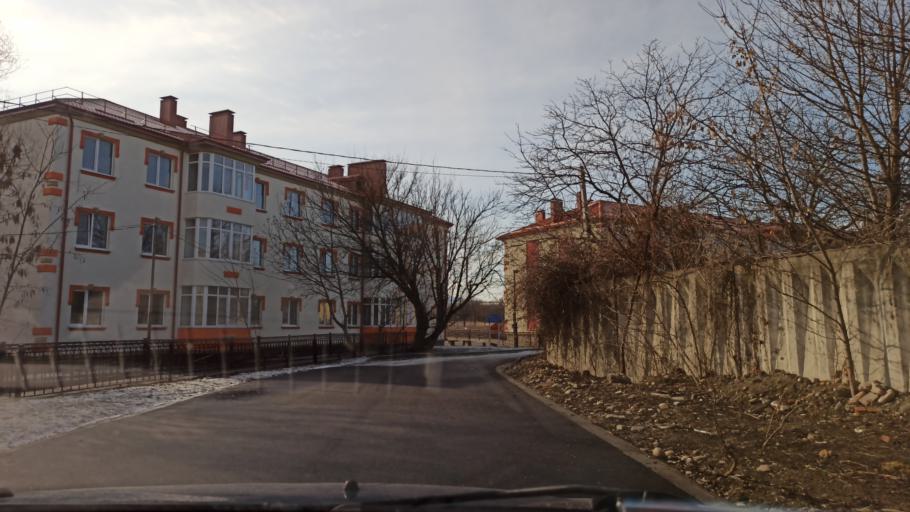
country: RU
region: Stavropol'skiy
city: Yessentukskaya
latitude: 44.0363
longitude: 42.8732
